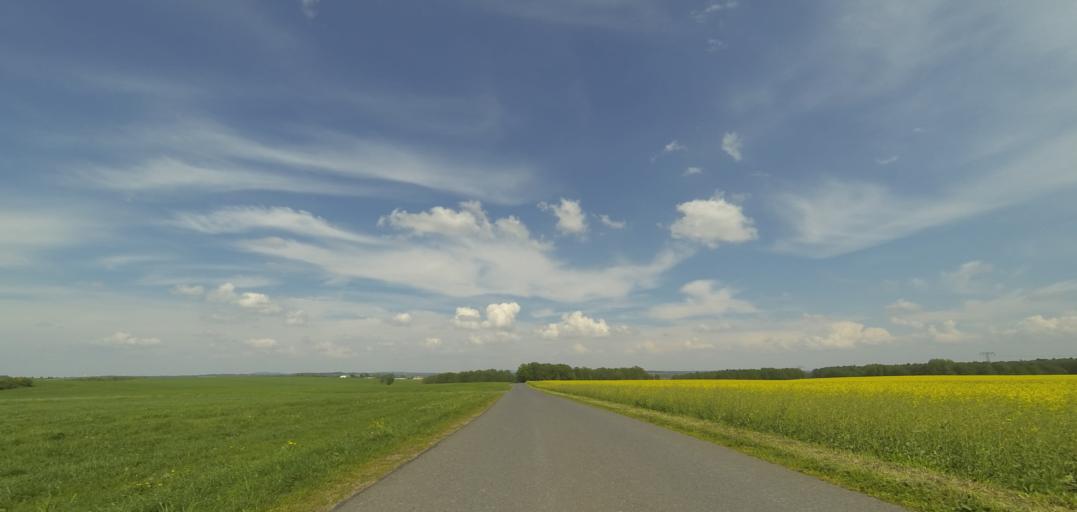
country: DE
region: Saxony
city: Radeberg
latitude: 51.0797
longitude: 13.9399
